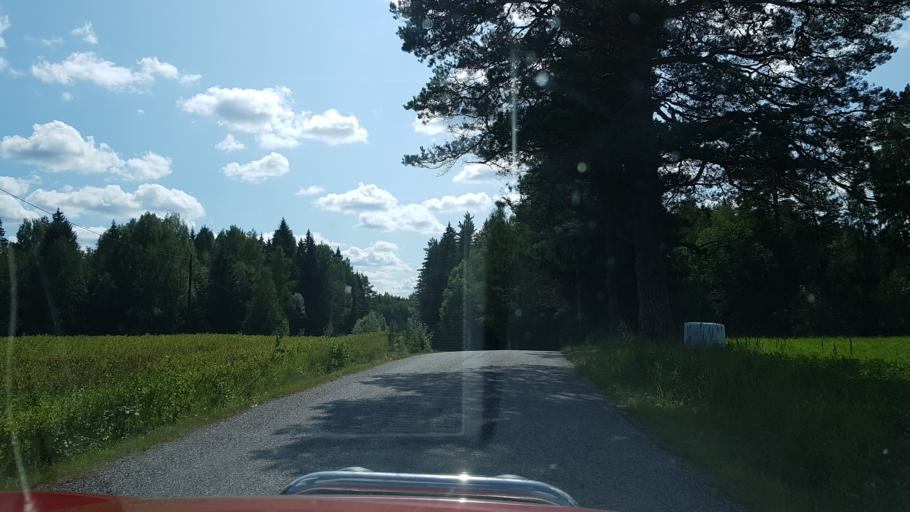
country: EE
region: Vorumaa
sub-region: Voru linn
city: Voru
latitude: 57.7301
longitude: 27.2098
